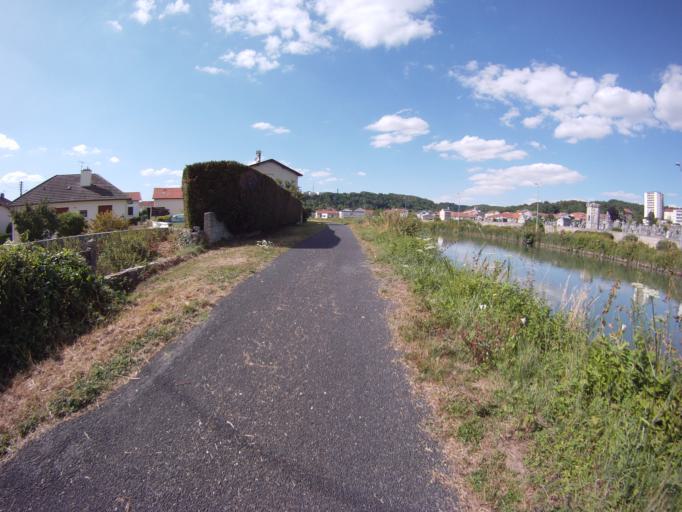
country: FR
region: Lorraine
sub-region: Departement de la Meuse
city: Bar-le-Duc
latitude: 48.7692
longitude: 5.1768
